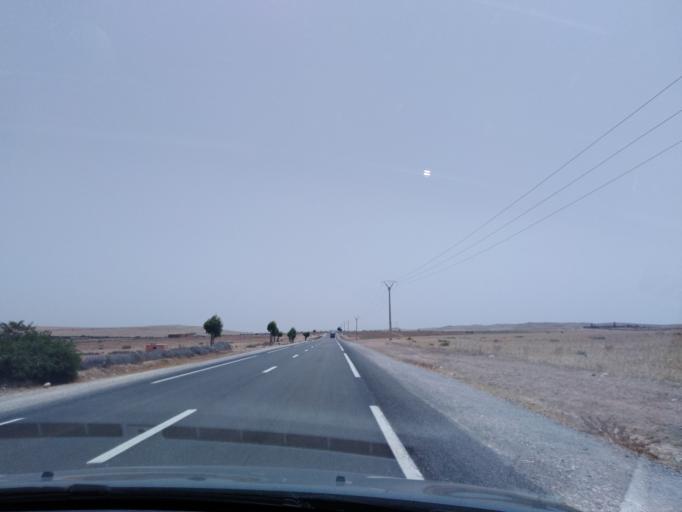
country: MA
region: Doukkala-Abda
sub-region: Safi
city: Youssoufia
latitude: 32.0401
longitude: -8.5263
